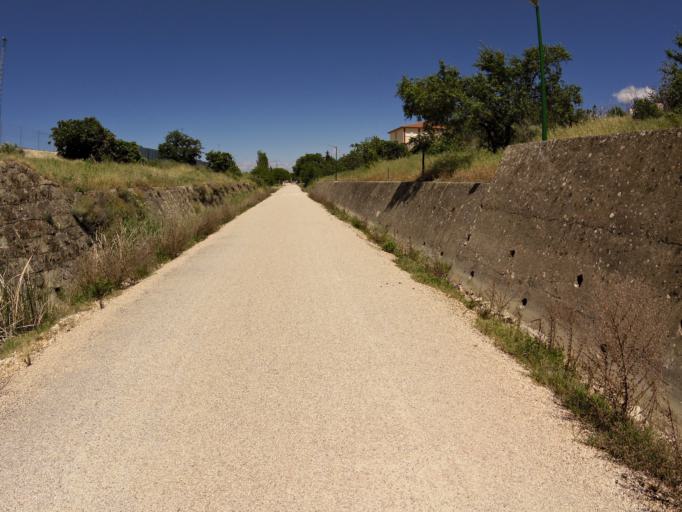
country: ES
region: Andalusia
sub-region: Provincia de Jaen
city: Torre del Campo
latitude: 37.7732
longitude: -3.9050
